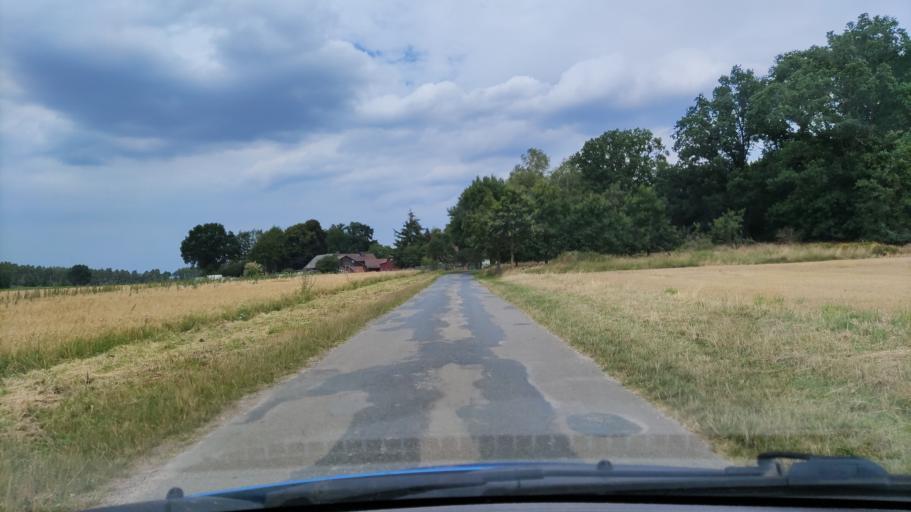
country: DE
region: Lower Saxony
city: Schnega
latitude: 52.9377
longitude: 10.8793
